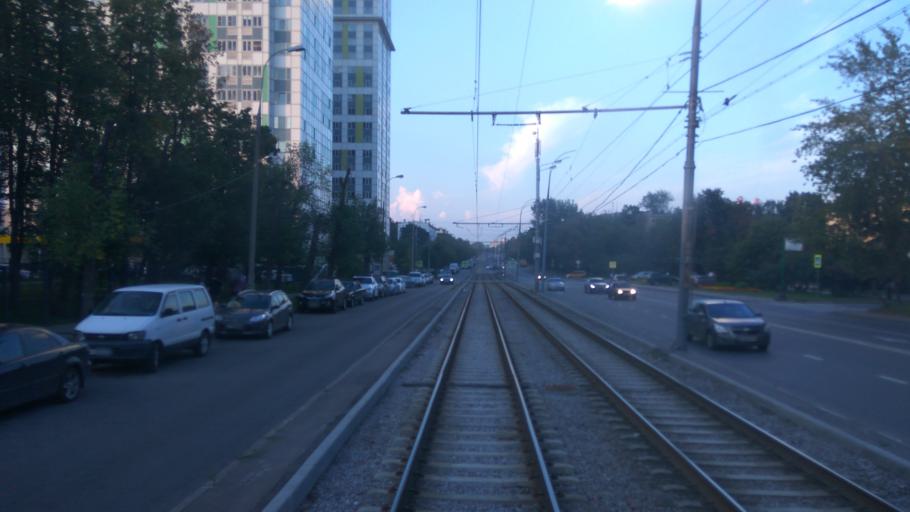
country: RU
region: Moskovskaya
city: Bogorodskoye
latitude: 55.8089
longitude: 37.7279
